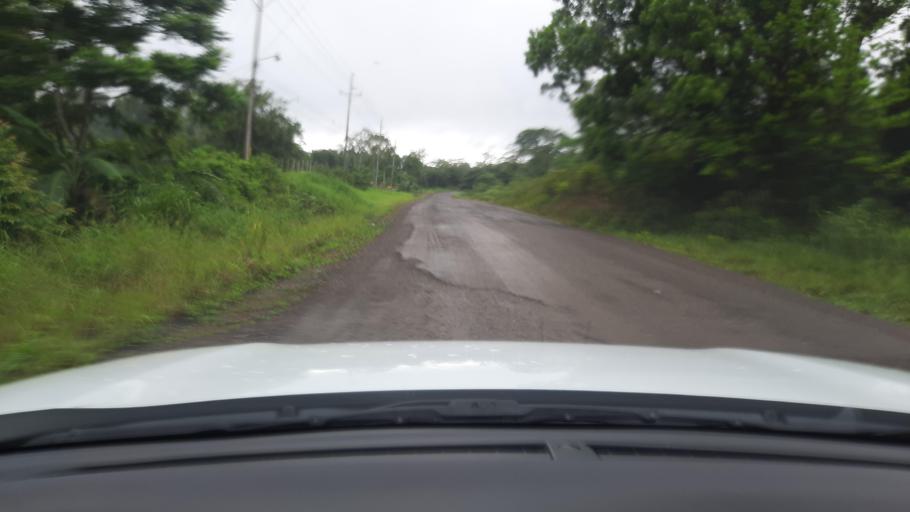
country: CR
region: Alajuela
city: San Jose
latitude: 11.0139
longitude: -85.3299
